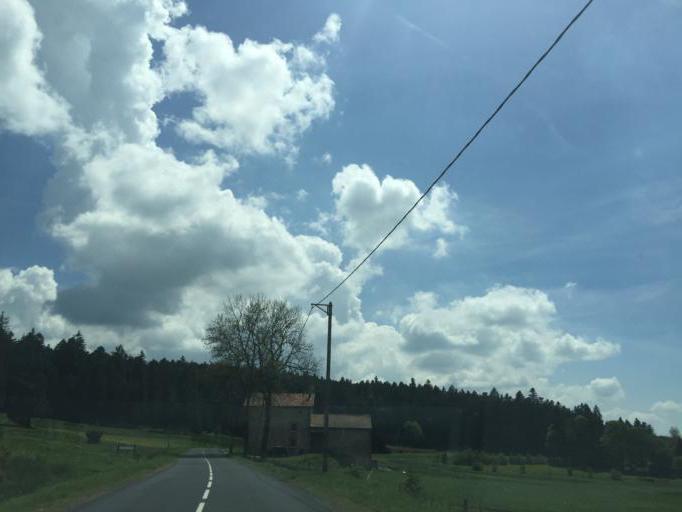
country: FR
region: Rhone-Alpes
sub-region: Departement de la Loire
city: Saint-Sauveur-en-Rue
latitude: 45.2979
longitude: 4.4560
